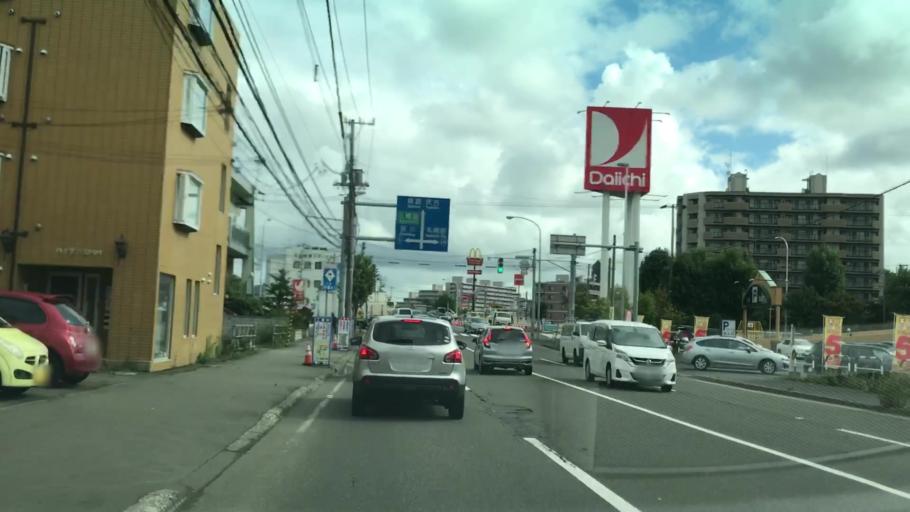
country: JP
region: Hokkaido
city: Sapporo
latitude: 43.0864
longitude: 141.3262
